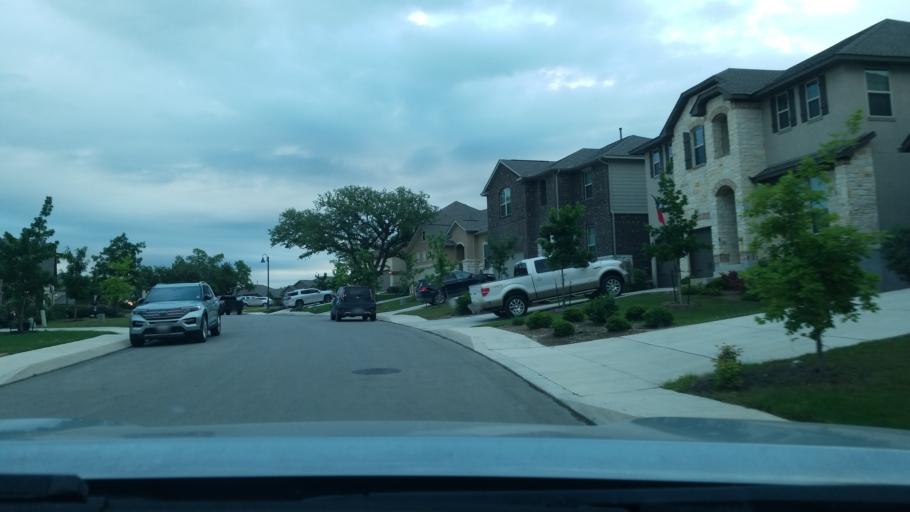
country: US
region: Texas
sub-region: Bexar County
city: Timberwood Park
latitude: 29.7161
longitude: -98.4564
